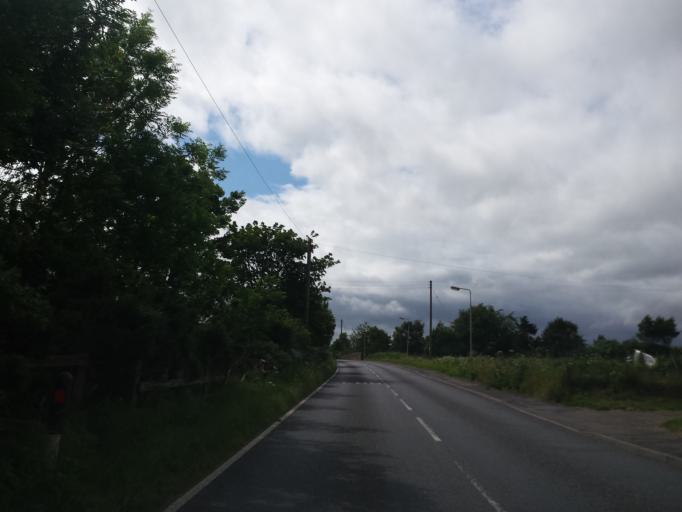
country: GB
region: Scotland
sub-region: Highland
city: Fortrose
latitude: 57.4850
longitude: -4.0645
